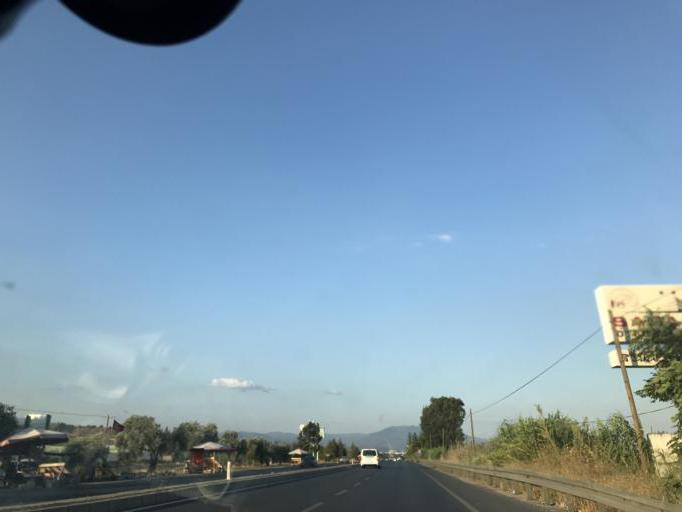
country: TR
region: Aydin
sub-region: Sultanhisar Ilcesi
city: Atca
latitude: 37.8871
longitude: 28.2244
